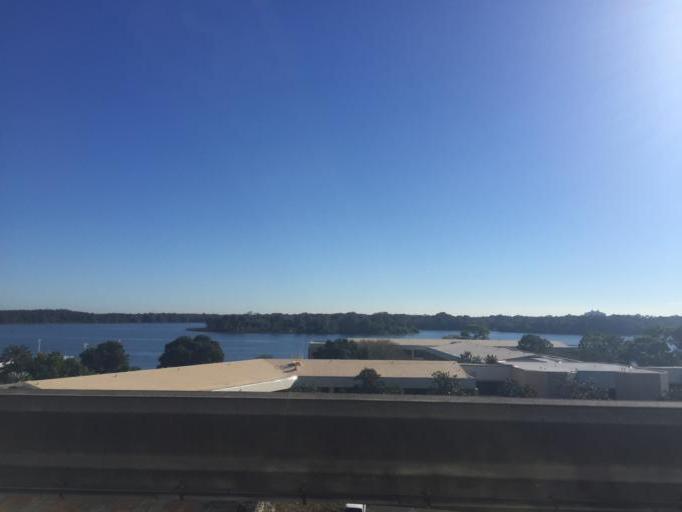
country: US
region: Florida
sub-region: Orange County
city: Bay Hill
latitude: 28.4141
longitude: -81.5745
